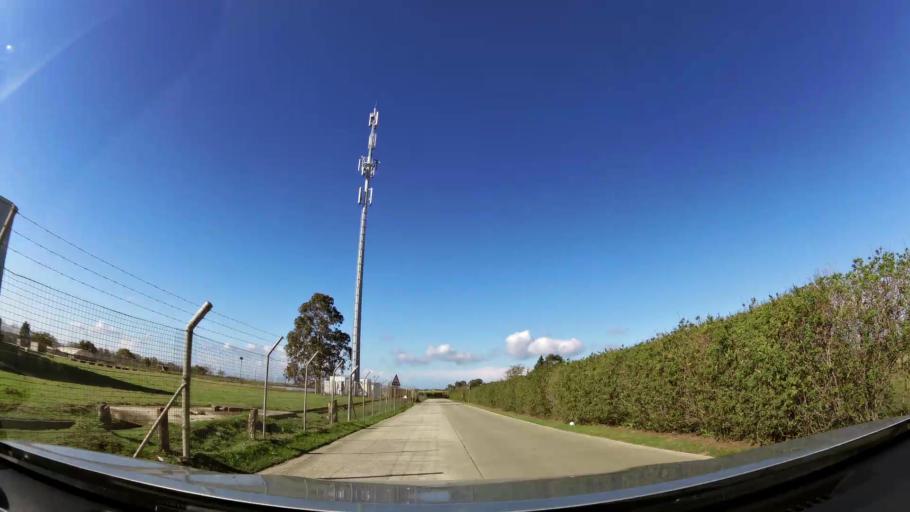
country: ZA
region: Western Cape
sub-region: Eden District Municipality
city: George
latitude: -33.9555
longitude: 22.3975
